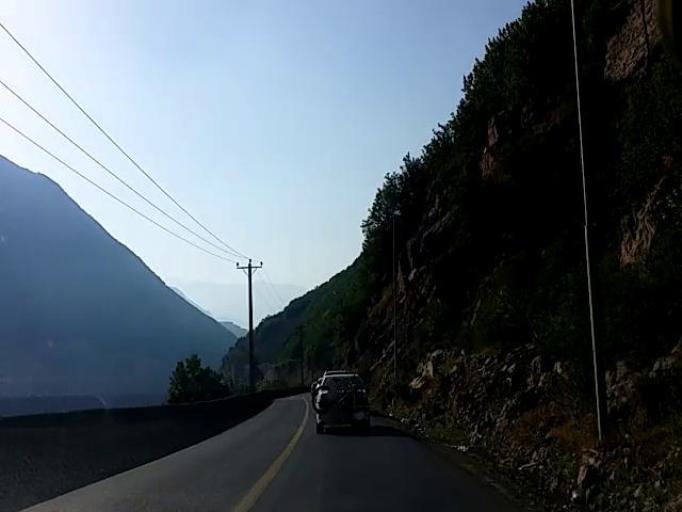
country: IR
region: Tehran
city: Tajrish
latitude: 36.2177
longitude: 51.3134
